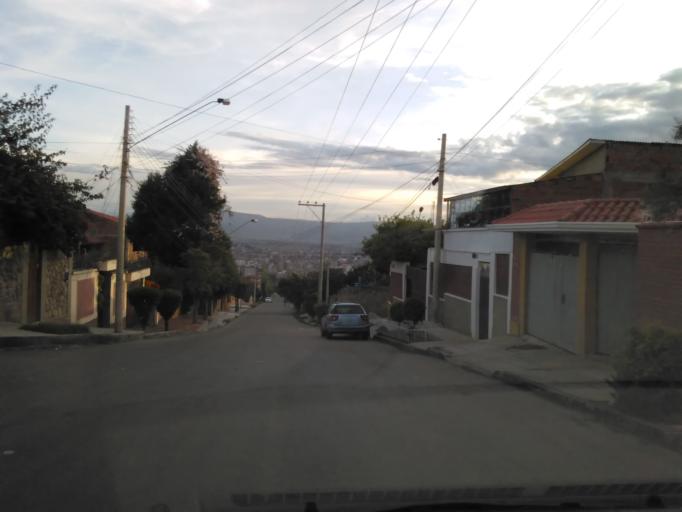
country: BO
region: Cochabamba
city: Cochabamba
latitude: -17.3539
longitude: -66.1590
